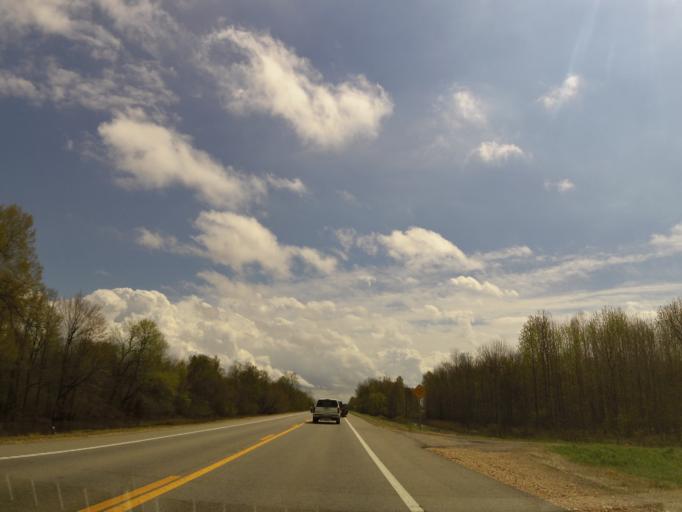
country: US
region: Arkansas
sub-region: Clay County
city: Corning
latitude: 36.4004
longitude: -90.5291
